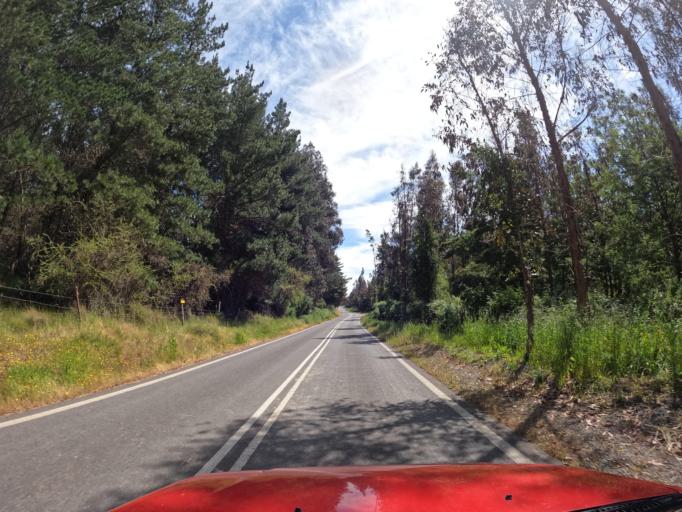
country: CL
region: Maule
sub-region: Provincia de Talca
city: Talca
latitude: -34.9927
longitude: -71.8703
